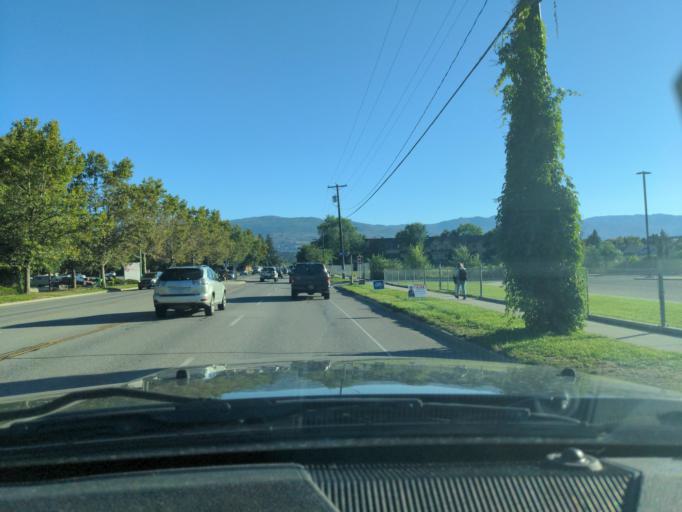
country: CA
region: British Columbia
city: Kelowna
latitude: 49.8598
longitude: -119.4745
